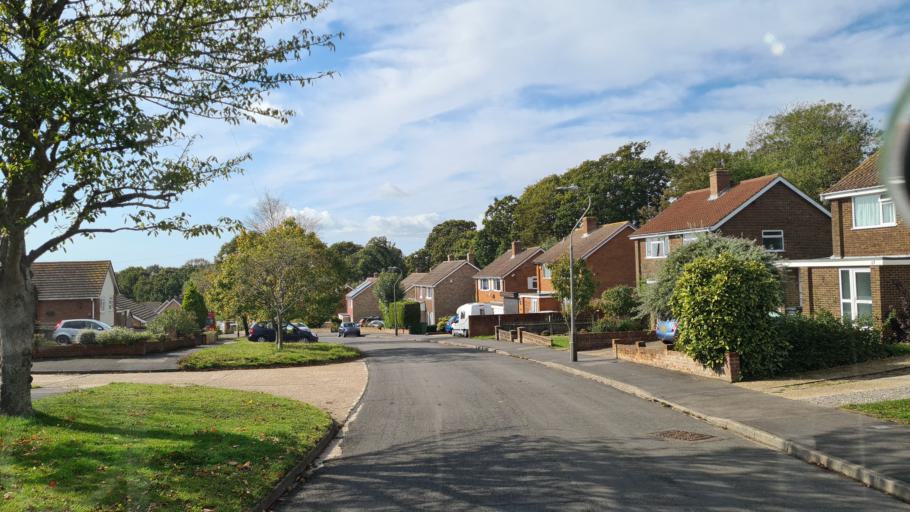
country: GB
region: England
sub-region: East Sussex
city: Hastings
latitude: 50.8787
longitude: 0.5655
